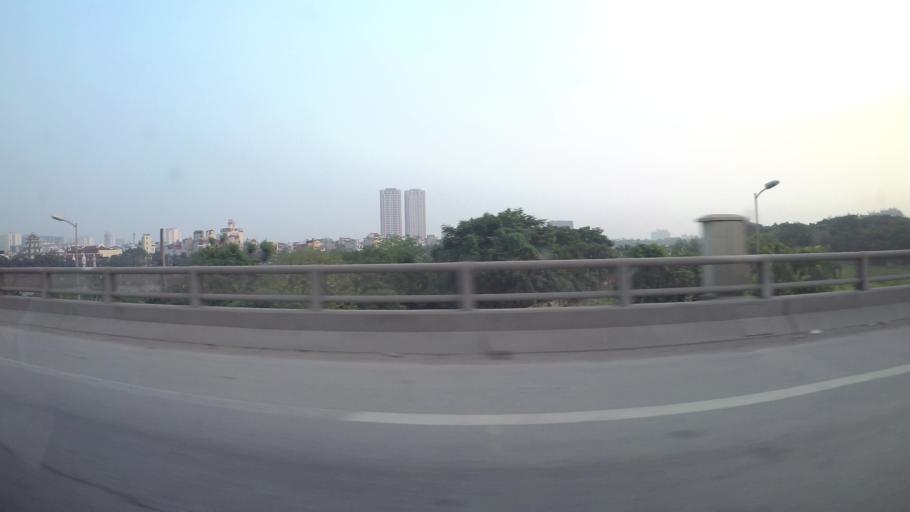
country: VN
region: Ha Noi
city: Van Dien
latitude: 20.9658
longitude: 105.8386
